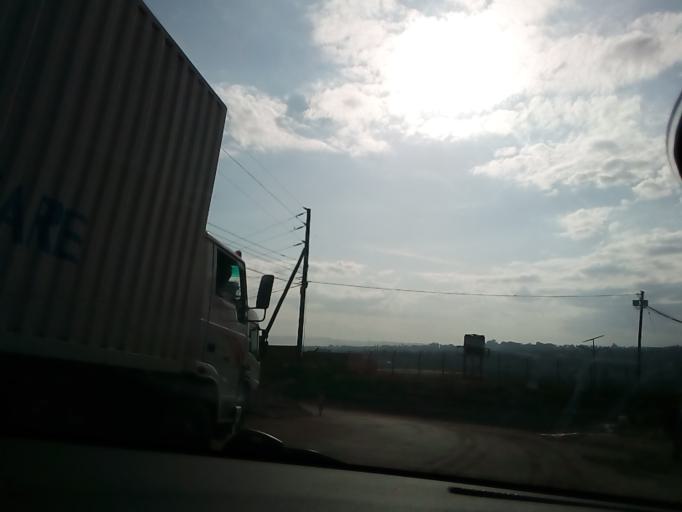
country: UG
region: Central Region
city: Masaka
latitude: -0.3416
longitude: 31.7394
